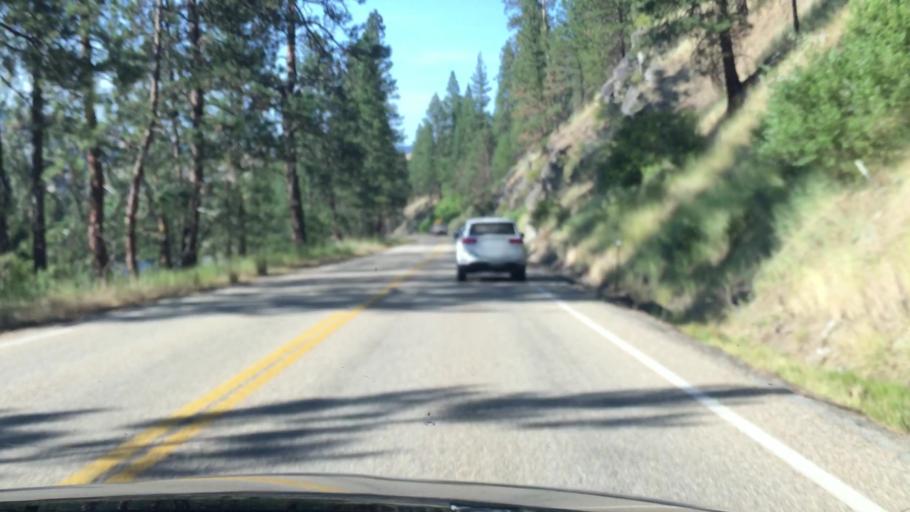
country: US
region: Idaho
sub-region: Boise County
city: Idaho City
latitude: 44.0637
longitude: -116.1217
